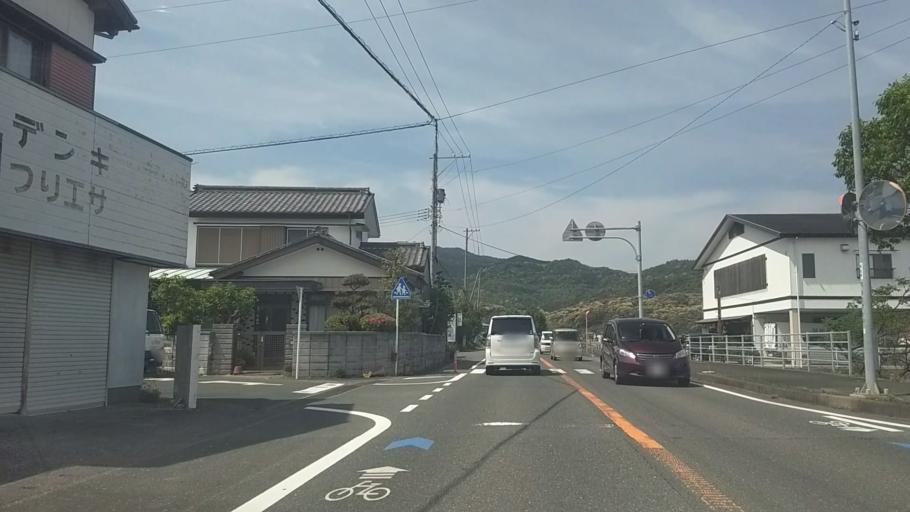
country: JP
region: Shizuoka
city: Kosai-shi
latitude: 34.7964
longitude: 137.6203
